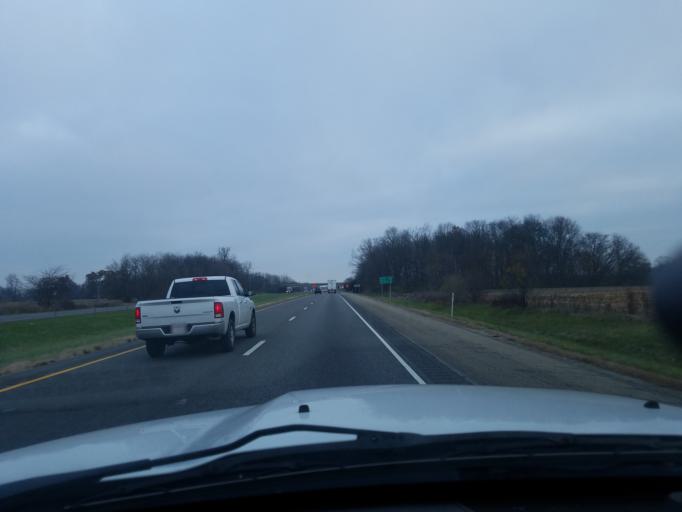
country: US
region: Indiana
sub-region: Delaware County
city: Daleville
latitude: 40.1307
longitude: -85.5682
